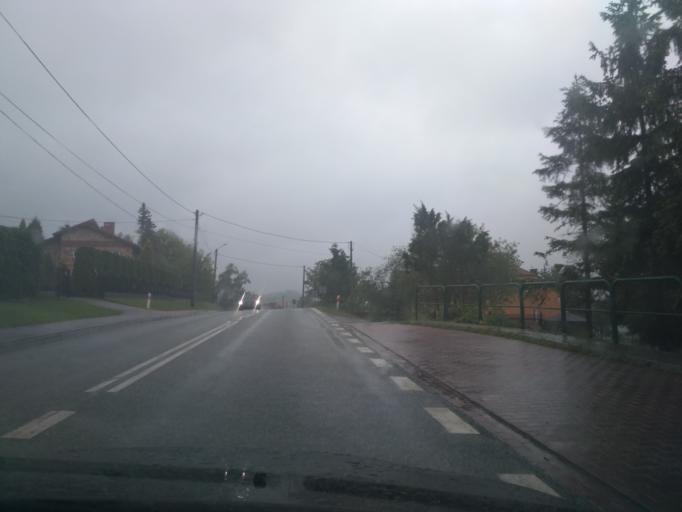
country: PL
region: Subcarpathian Voivodeship
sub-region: Powiat jasielski
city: Debowiec
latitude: 49.7043
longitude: 21.4736
